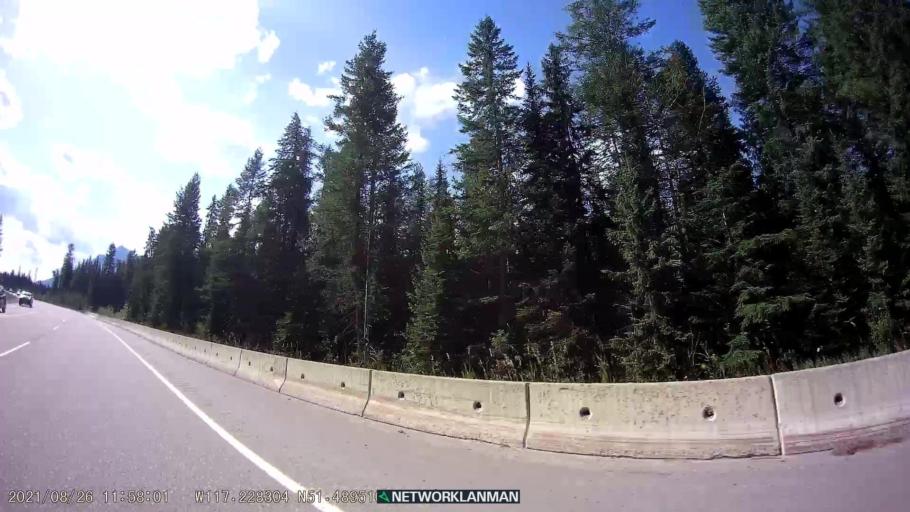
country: CA
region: British Columbia
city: Golden
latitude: 51.4889
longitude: -117.2284
